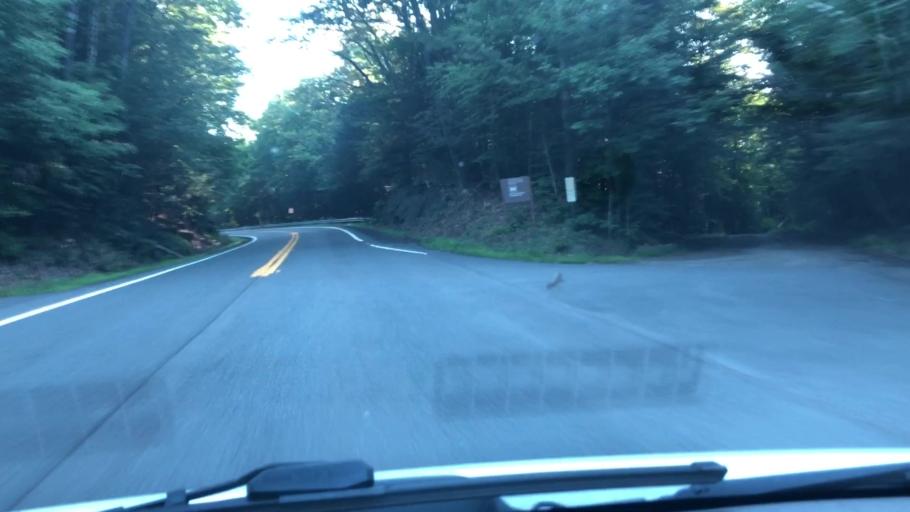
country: US
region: Massachusetts
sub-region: Hampshire County
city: Westhampton
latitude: 42.2922
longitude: -72.8710
